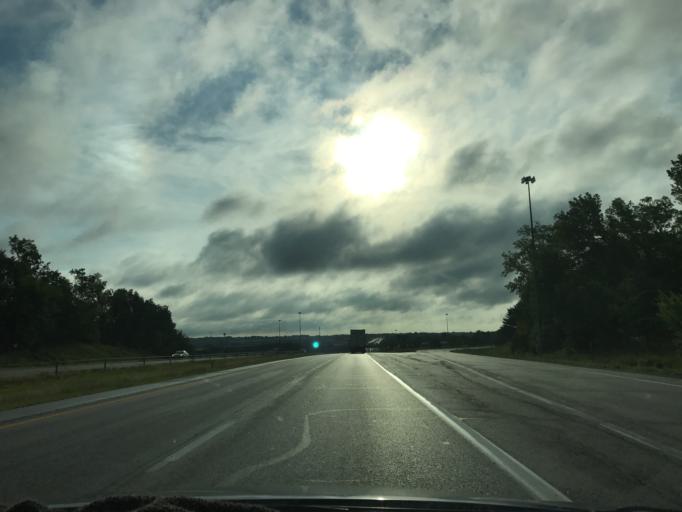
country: US
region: Iowa
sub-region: Johnson County
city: Tiffin
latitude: 41.6942
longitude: -91.6459
